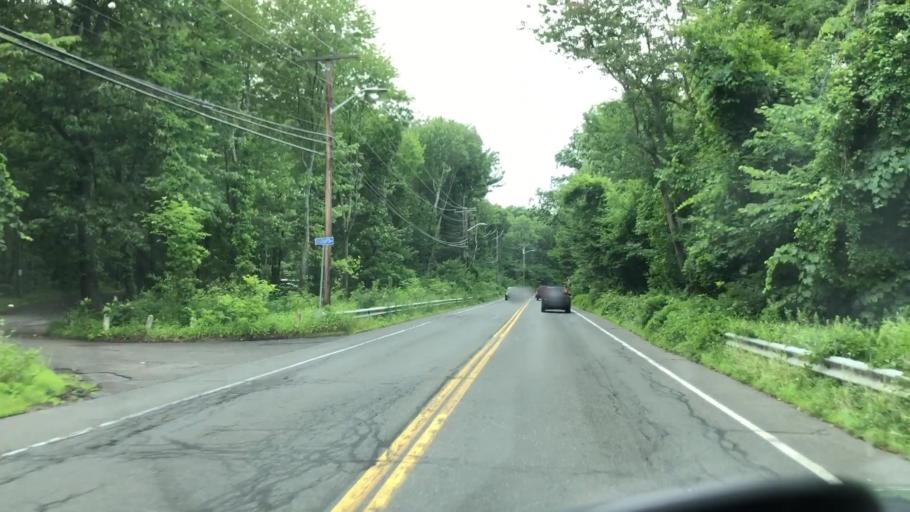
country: US
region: Massachusetts
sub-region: Hampden County
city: Holyoke
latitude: 42.2241
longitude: -72.6442
